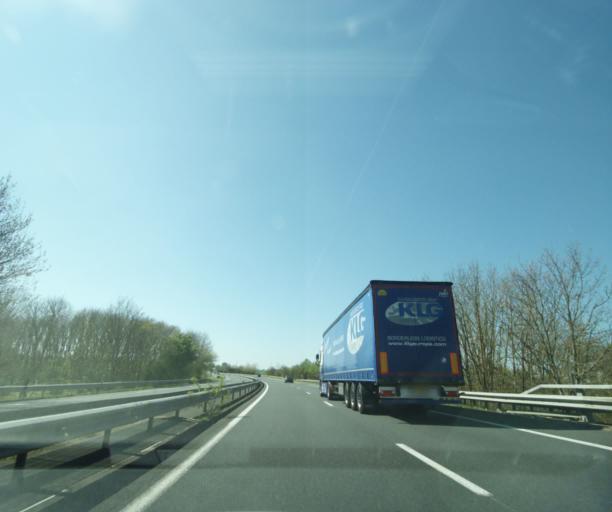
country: FR
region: Centre
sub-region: Departement de l'Indre
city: Vatan
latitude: 47.0476
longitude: 1.7987
